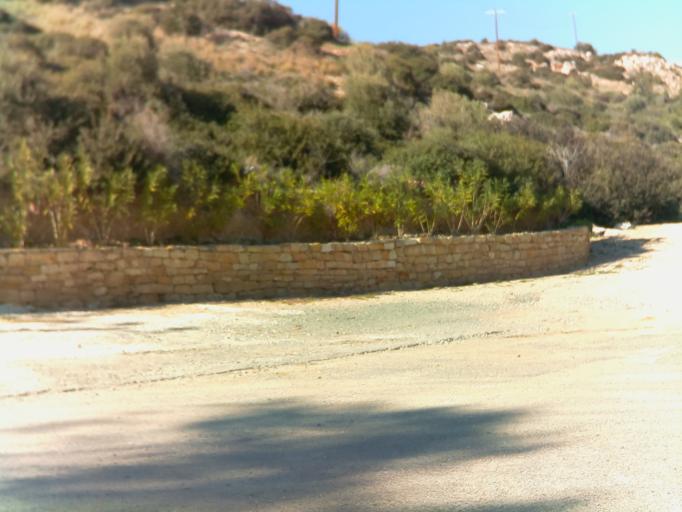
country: CY
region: Limassol
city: Pissouri
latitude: 34.6657
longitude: 32.6278
